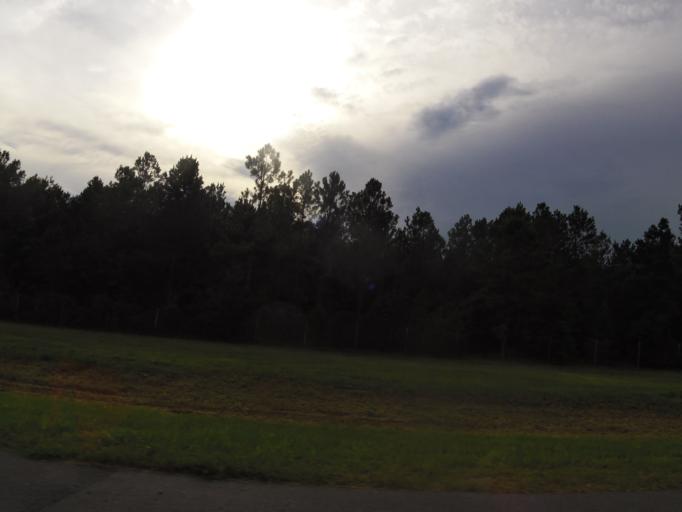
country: US
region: Florida
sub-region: Clay County
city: Middleburg
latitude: 30.1083
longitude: -81.8351
